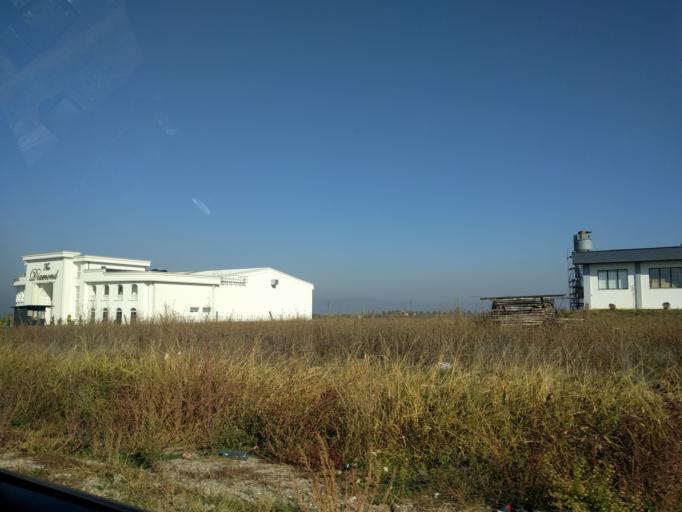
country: XK
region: Prizren
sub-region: Prizren
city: Prizren
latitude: 42.2435
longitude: 20.7480
